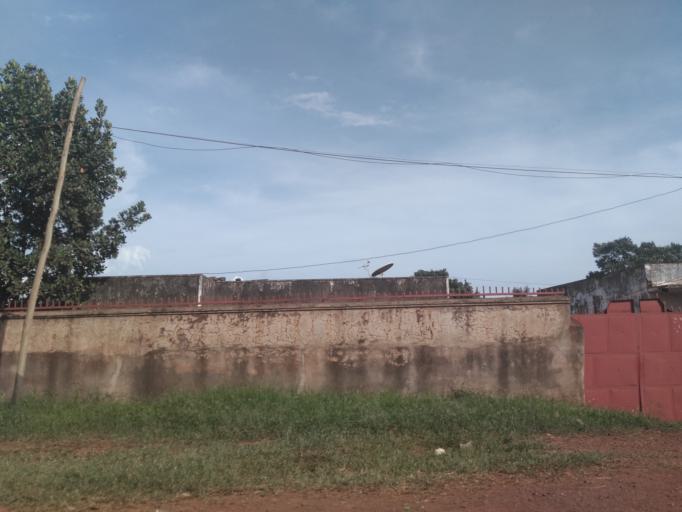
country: UG
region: Eastern Region
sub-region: Jinja District
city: Jinja
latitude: 0.4358
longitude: 33.2094
